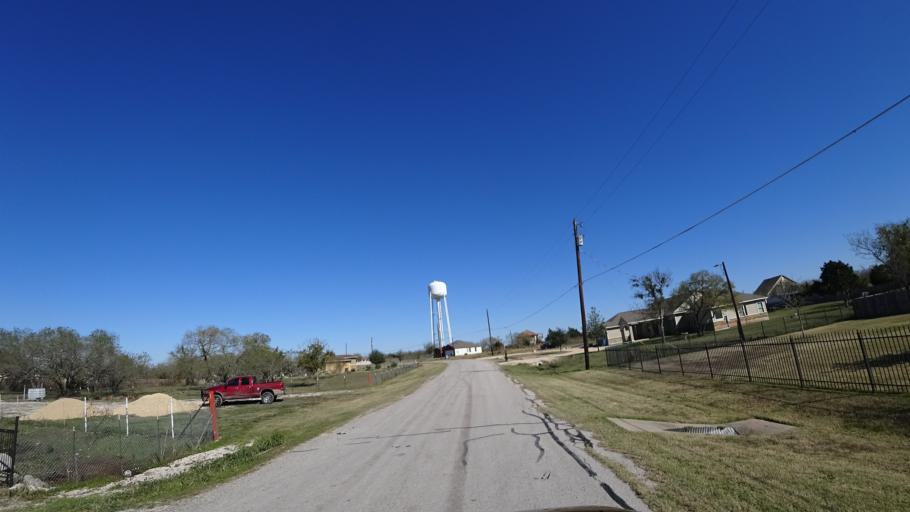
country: US
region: Texas
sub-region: Travis County
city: Garfield
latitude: 30.0979
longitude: -97.6009
